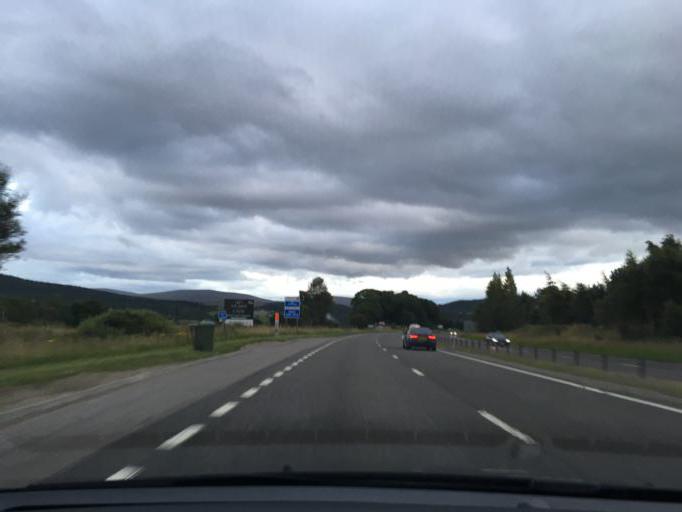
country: GB
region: Scotland
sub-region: Highland
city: Inverness
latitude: 57.4342
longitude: -4.1326
